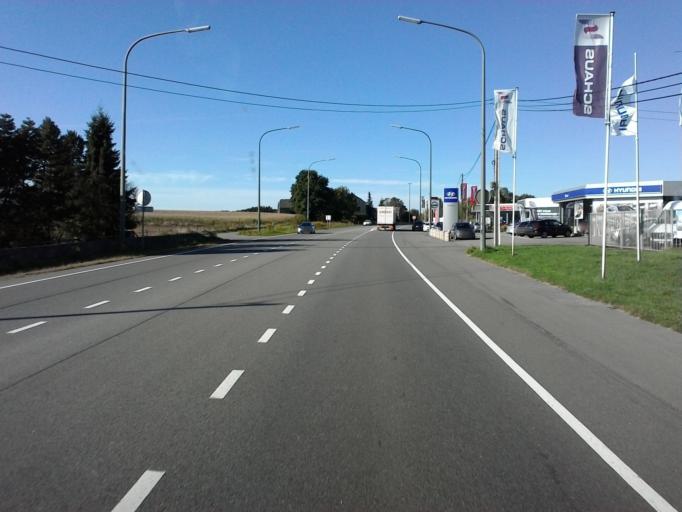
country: BE
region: Wallonia
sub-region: Province du Luxembourg
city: Arlon
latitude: 49.7113
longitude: 5.8023
